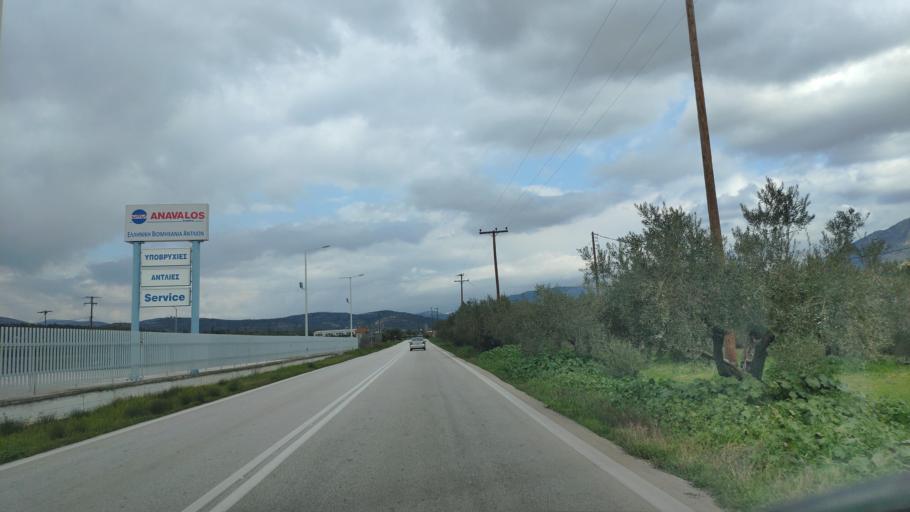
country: GR
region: Peloponnese
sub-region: Nomos Argolidos
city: Koutsopodi
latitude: 37.7052
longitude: 22.7239
